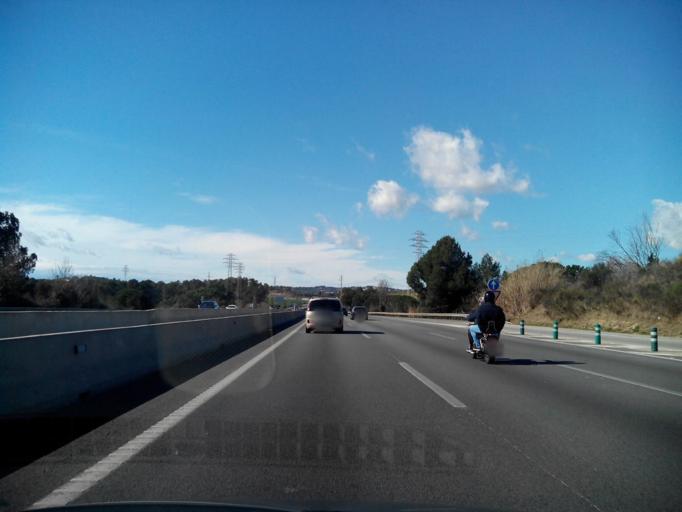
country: ES
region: Catalonia
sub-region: Provincia de Barcelona
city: Sant Quirze del Valles
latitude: 41.5435
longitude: 2.0670
